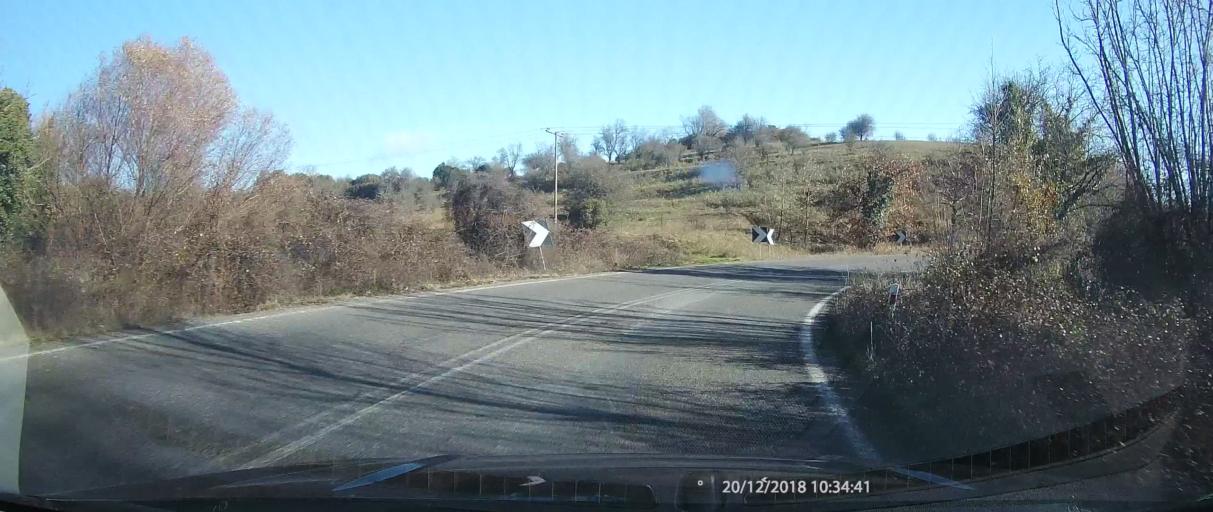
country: GR
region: Peloponnese
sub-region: Nomos Lakonias
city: Kariai
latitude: 37.3525
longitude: 22.4105
